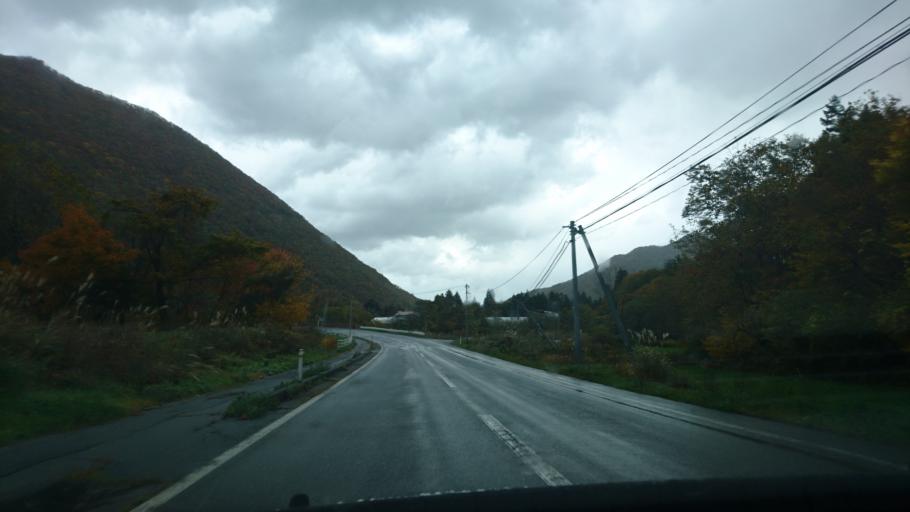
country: JP
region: Iwate
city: Shizukuishi
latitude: 39.6038
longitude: 140.9305
